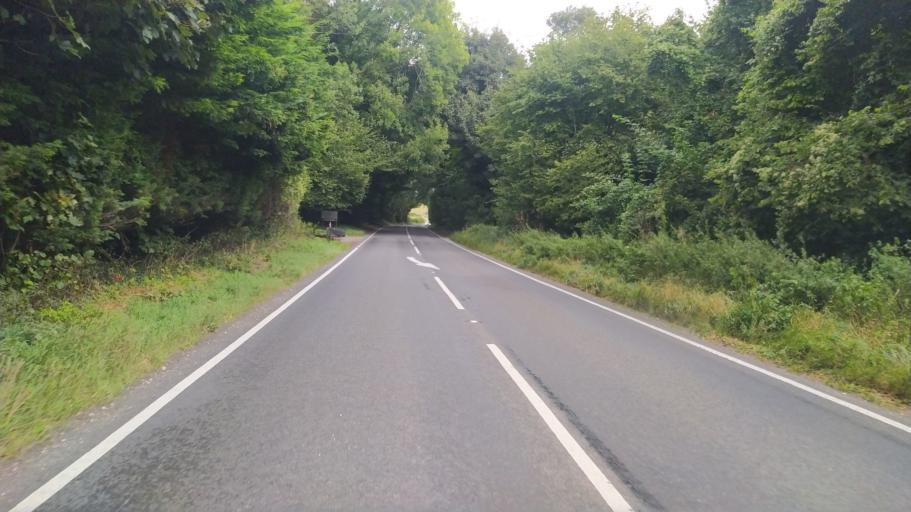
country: GB
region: England
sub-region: Dorset
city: Blandford Forum
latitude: 50.9115
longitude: -2.0617
